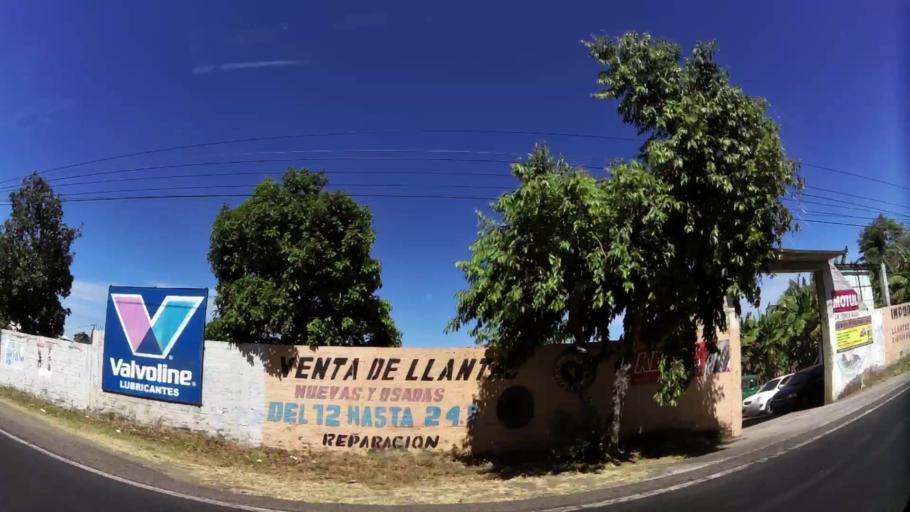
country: SV
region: Ahuachapan
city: Ahuachapan
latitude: 13.9321
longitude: -89.8349
